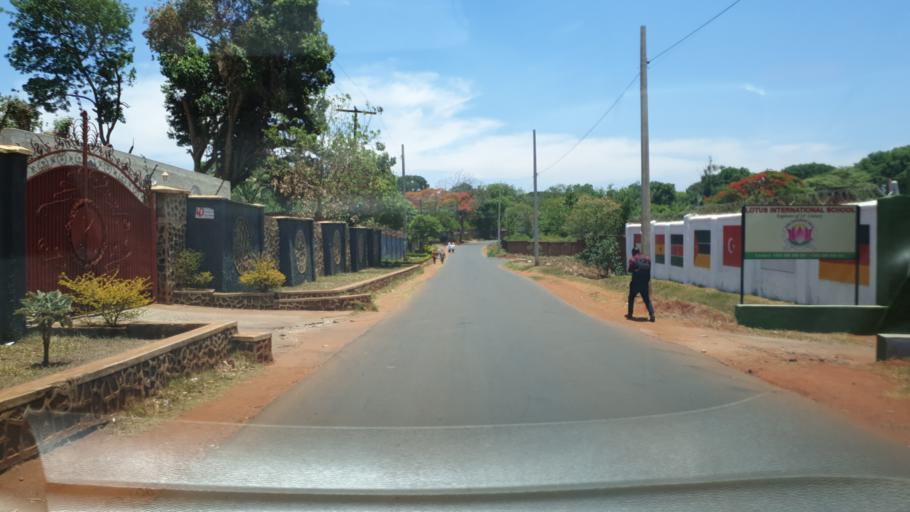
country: MW
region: Central Region
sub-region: Lilongwe District
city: Lilongwe
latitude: -13.9834
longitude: 33.7532
